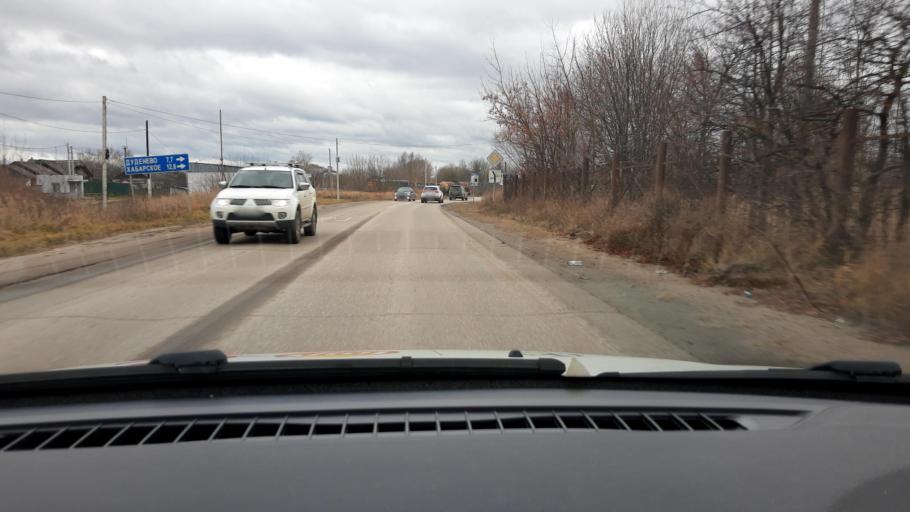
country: RU
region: Nizjnij Novgorod
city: Bogorodsk
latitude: 56.1155
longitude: 43.5294
